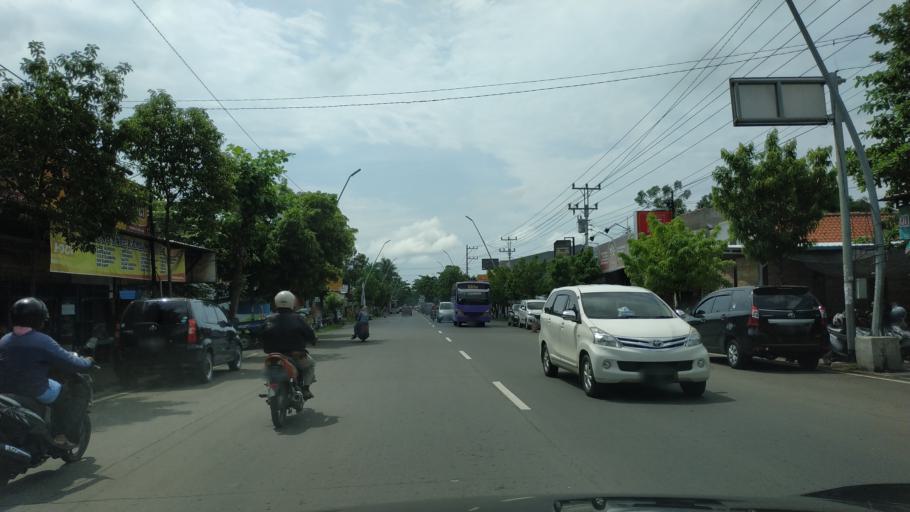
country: ID
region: Central Java
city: Tegal
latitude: -6.8821
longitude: 109.1264
